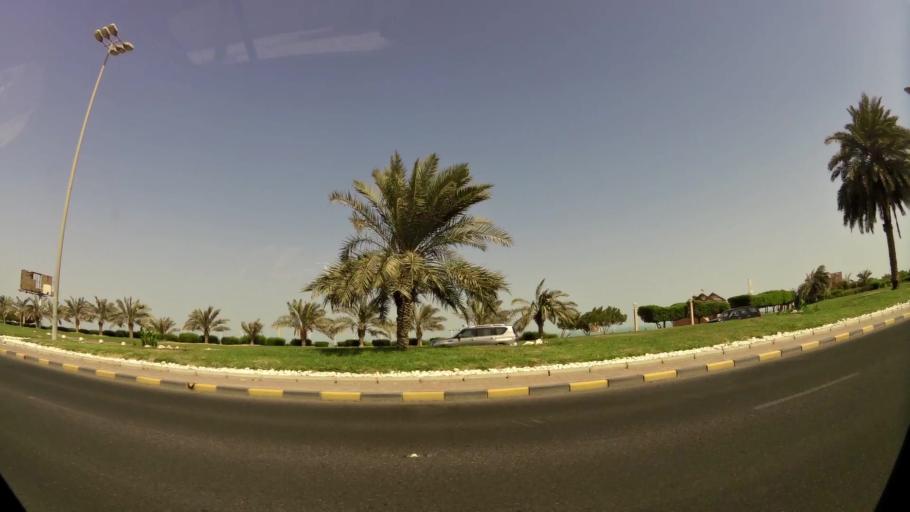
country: KW
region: Muhafazat Hawalli
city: Hawalli
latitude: 29.3471
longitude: 48.0388
